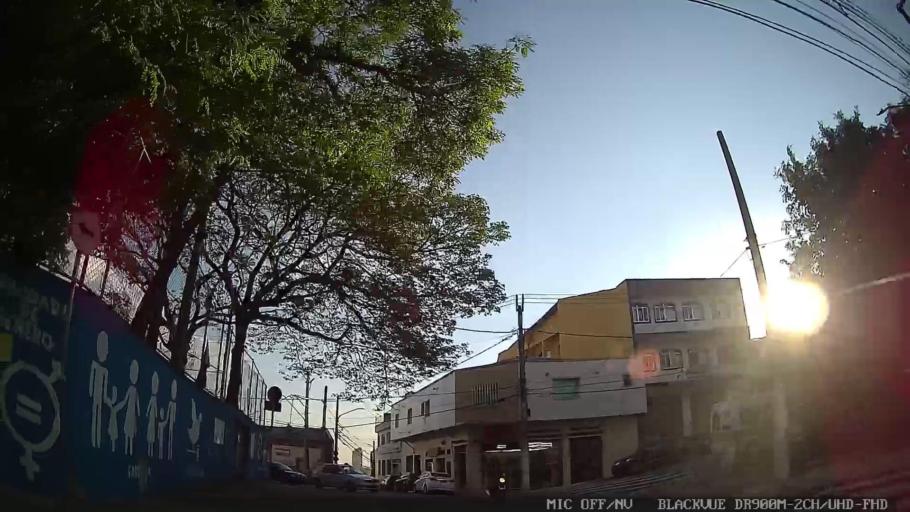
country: BR
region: Sao Paulo
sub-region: Sao Caetano Do Sul
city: Sao Caetano do Sul
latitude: -23.5812
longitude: -46.5382
